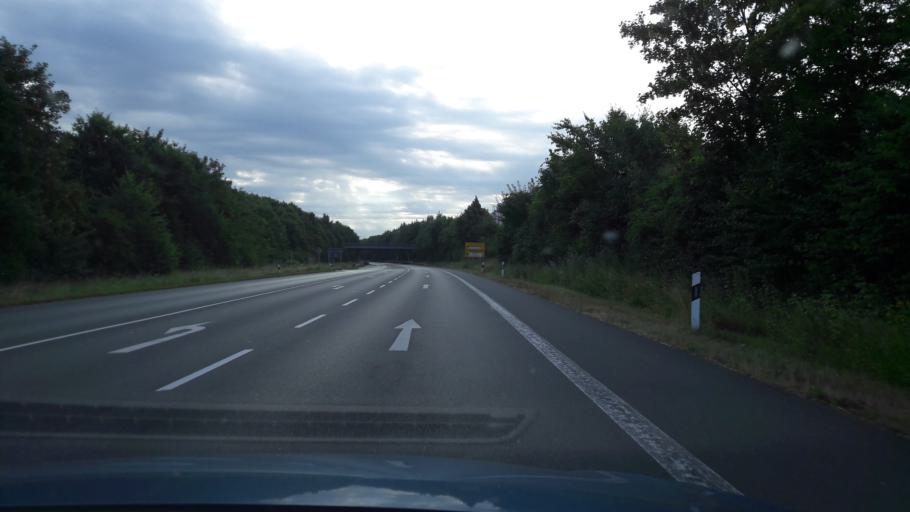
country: DE
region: North Rhine-Westphalia
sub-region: Regierungsbezirk Munster
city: Everswinkel
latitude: 51.9291
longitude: 7.8292
